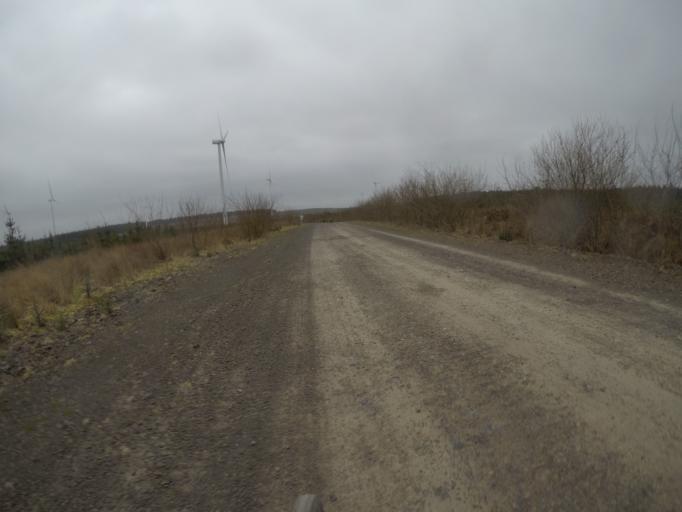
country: GB
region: Scotland
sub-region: East Ayrshire
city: Newmilns
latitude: 55.6515
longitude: -4.3252
